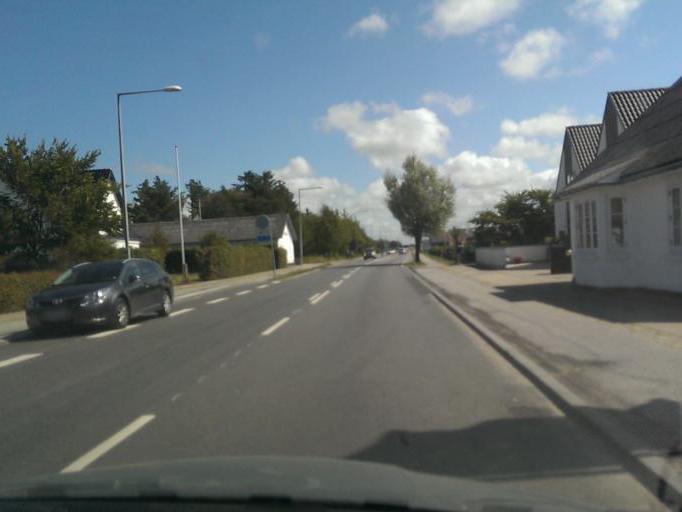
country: DK
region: North Denmark
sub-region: Jammerbugt Kommune
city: Pandrup
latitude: 57.2485
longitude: 9.6169
